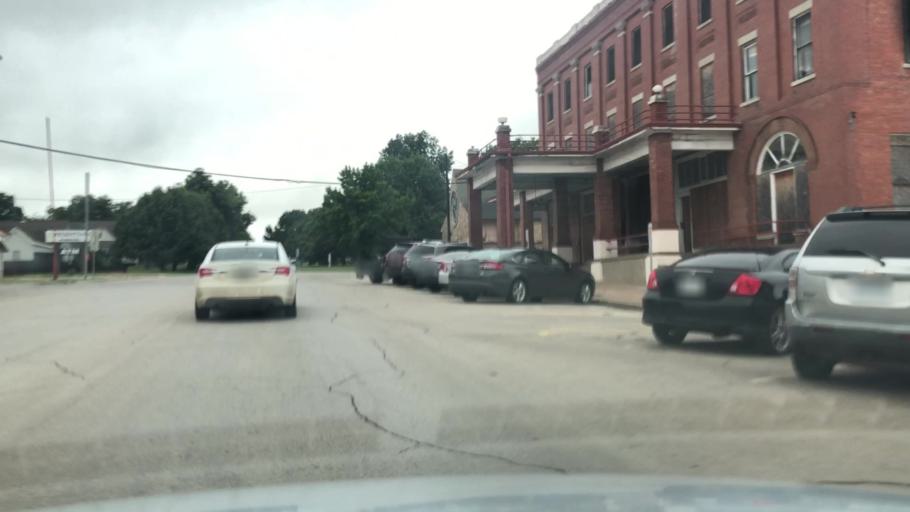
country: US
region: Oklahoma
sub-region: Nowata County
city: Nowata
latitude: 36.7015
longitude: -95.6387
